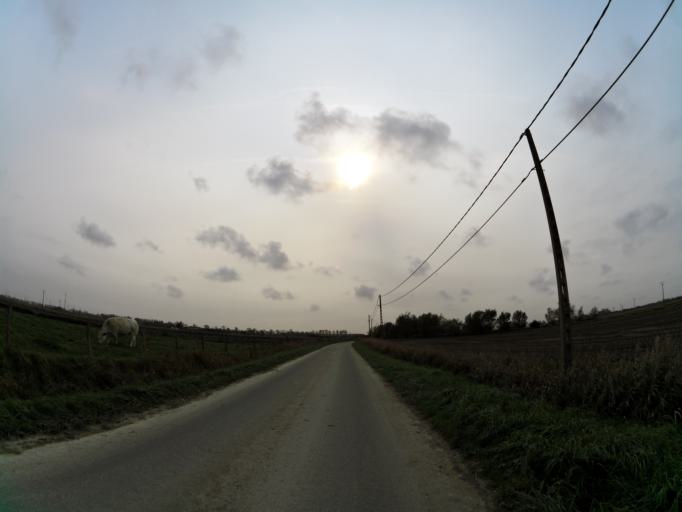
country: BE
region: Flanders
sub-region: Provincie West-Vlaanderen
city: Oudenburg
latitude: 51.2188
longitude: 3.0199
